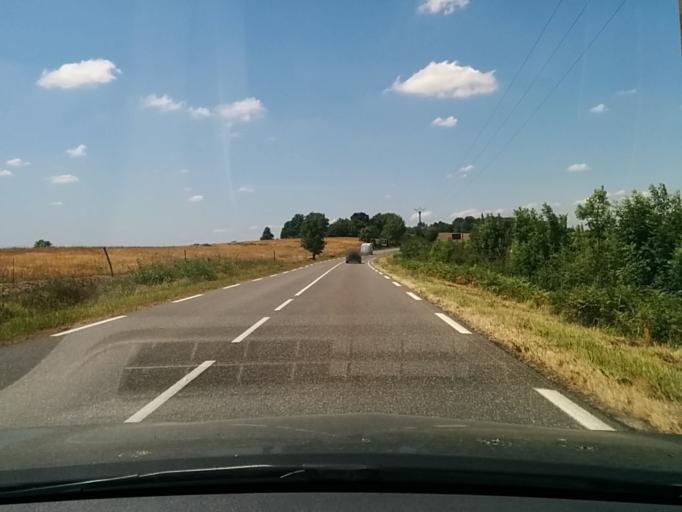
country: FR
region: Midi-Pyrenees
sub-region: Departement du Gers
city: Eauze
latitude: 43.7867
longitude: 0.1084
